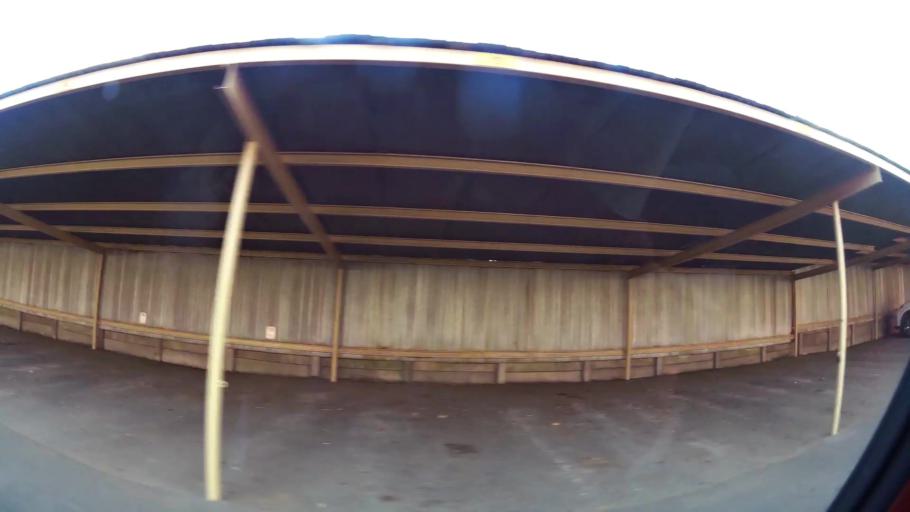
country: ZA
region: North-West
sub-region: Dr Kenneth Kaunda District Municipality
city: Potchefstroom
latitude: -26.6844
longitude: 27.0923
